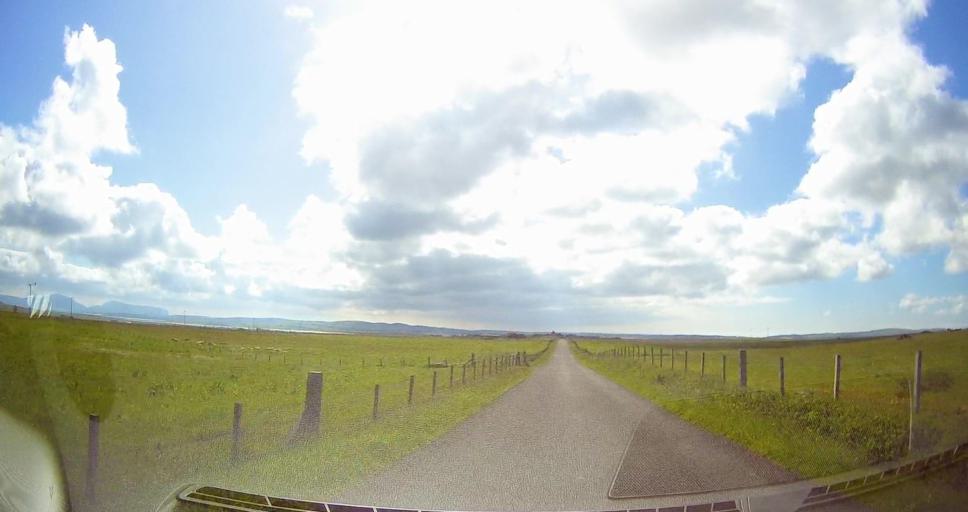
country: GB
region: Scotland
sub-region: Orkney Islands
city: Stromness
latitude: 59.0452
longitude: -3.1678
